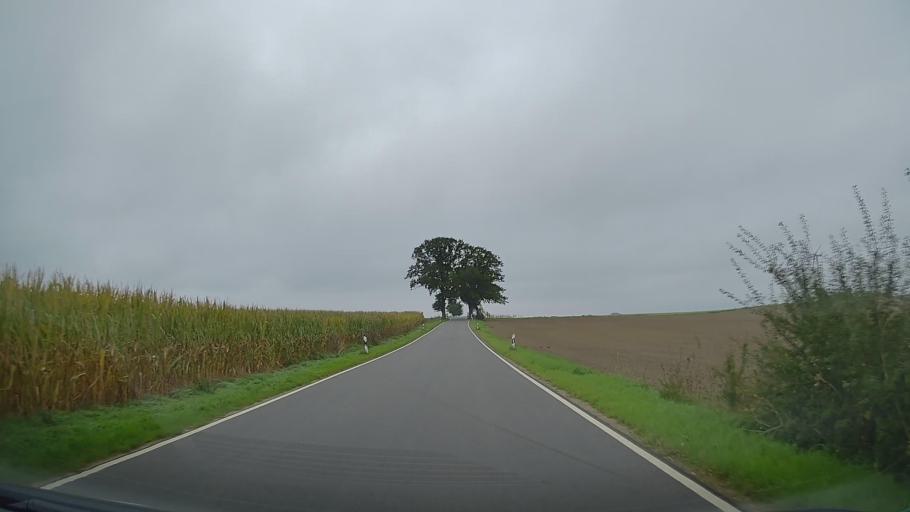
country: DE
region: Mecklenburg-Vorpommern
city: Dummerstorf
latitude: 53.9663
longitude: 12.2443
